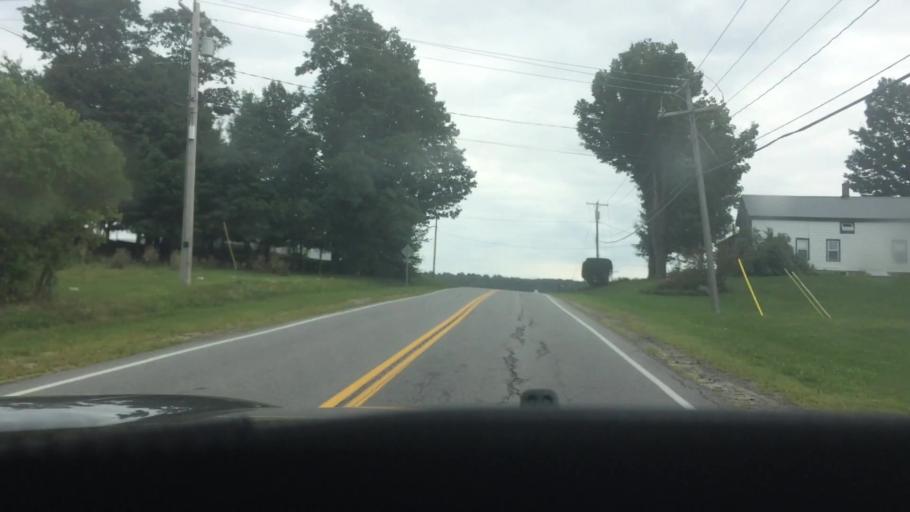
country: US
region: New York
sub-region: St. Lawrence County
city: Canton
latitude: 44.5553
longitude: -75.1122
